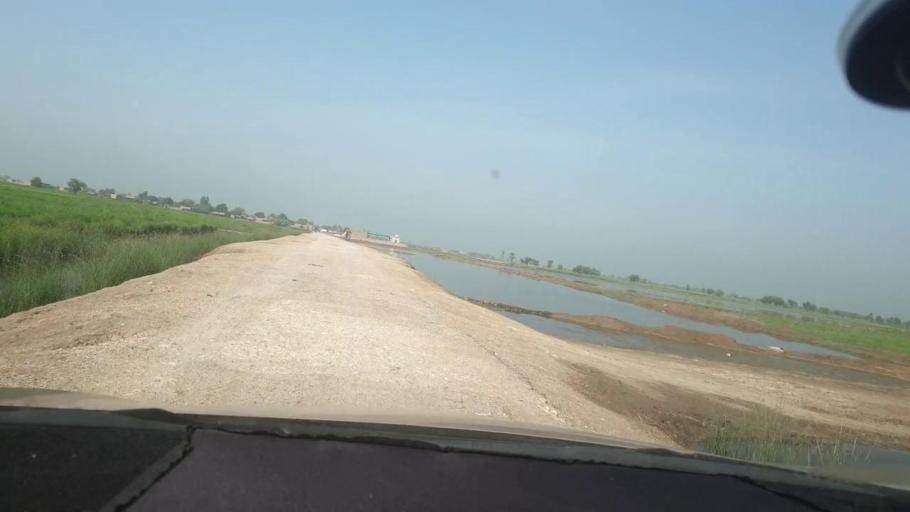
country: PK
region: Sindh
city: Miro Khan
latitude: 27.7377
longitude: 68.0171
